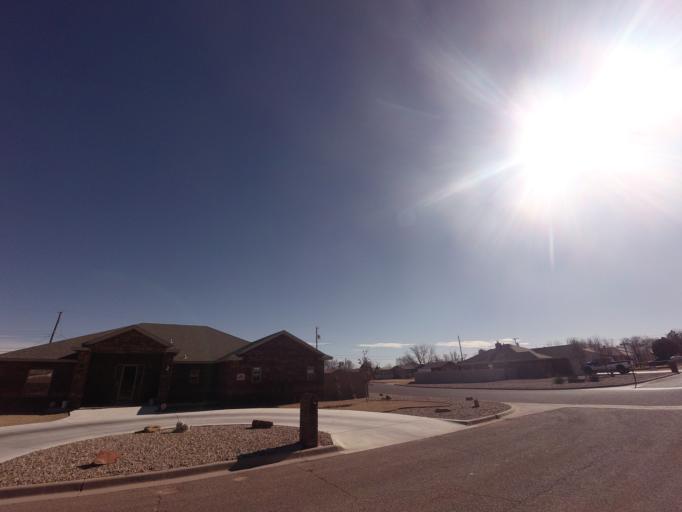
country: US
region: New Mexico
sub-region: Curry County
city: Clovis
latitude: 34.4106
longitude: -103.2282
